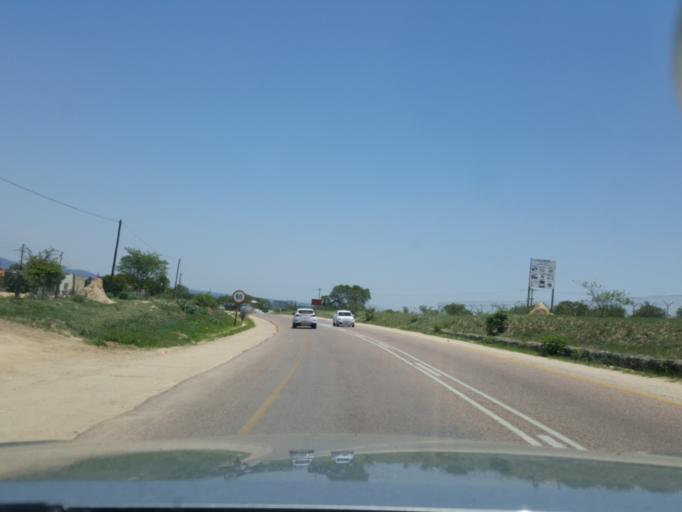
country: ZA
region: Limpopo
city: Thulamahashi
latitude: -24.5956
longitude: 31.0459
